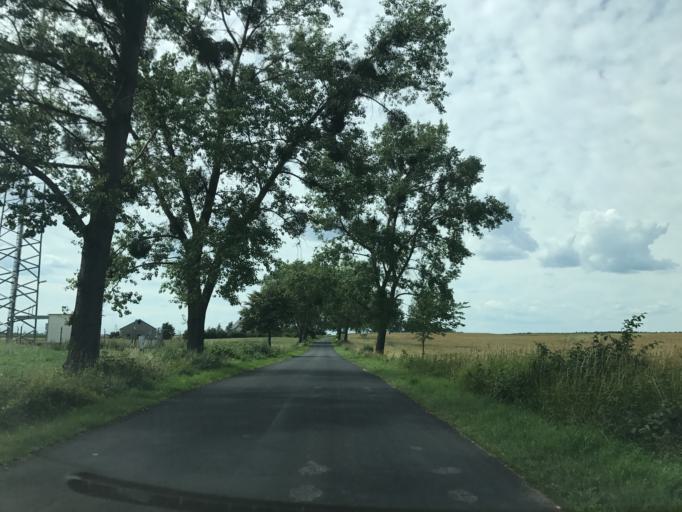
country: PL
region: Kujawsko-Pomorskie
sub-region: Powiat brodnicki
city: Gorzno
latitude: 53.2043
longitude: 19.6348
